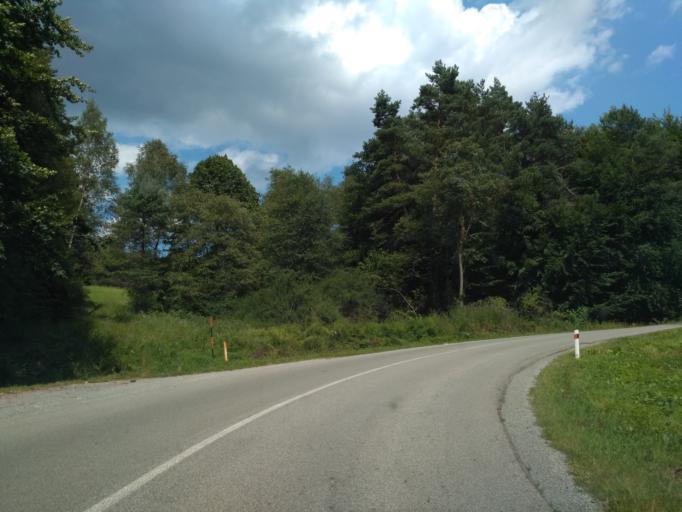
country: SK
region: Kosicky
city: Gelnica
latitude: 48.9270
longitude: 21.0407
